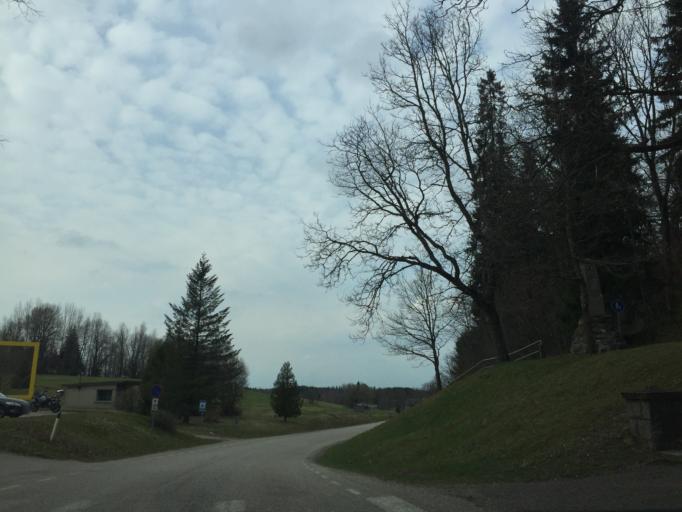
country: EE
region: Vorumaa
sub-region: Voru linn
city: Voru
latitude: 57.7133
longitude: 27.0557
